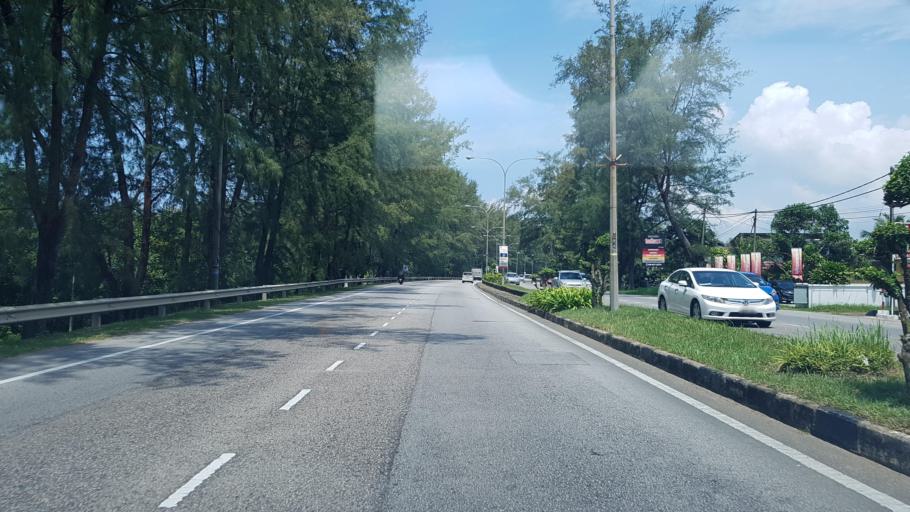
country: MY
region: Terengganu
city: Kuala Terengganu
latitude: 5.2931
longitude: 103.1676
